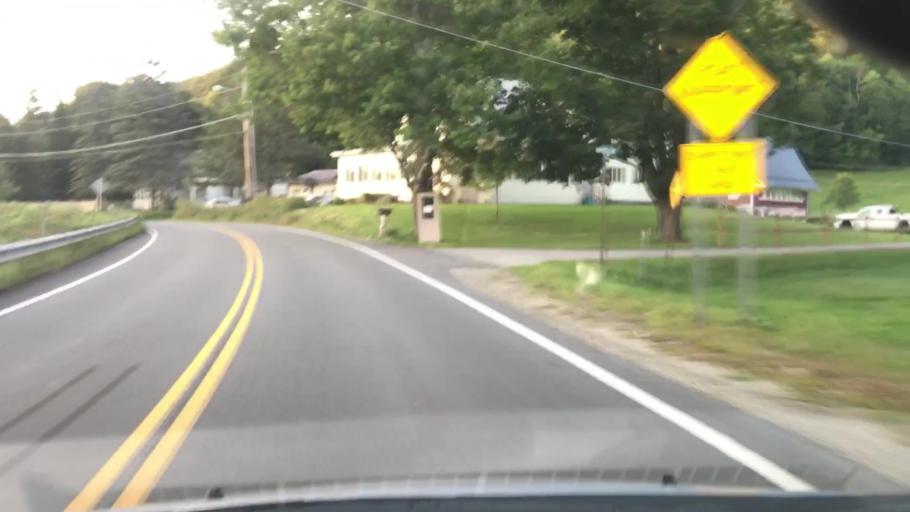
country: US
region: New Hampshire
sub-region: Grafton County
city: Woodsville
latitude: 44.1561
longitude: -72.0367
